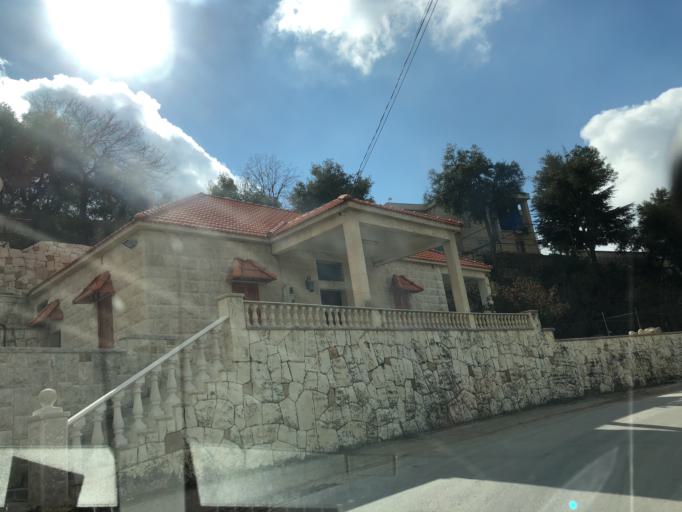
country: LB
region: Liban-Nord
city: Amioun
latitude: 34.2016
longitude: 35.8216
